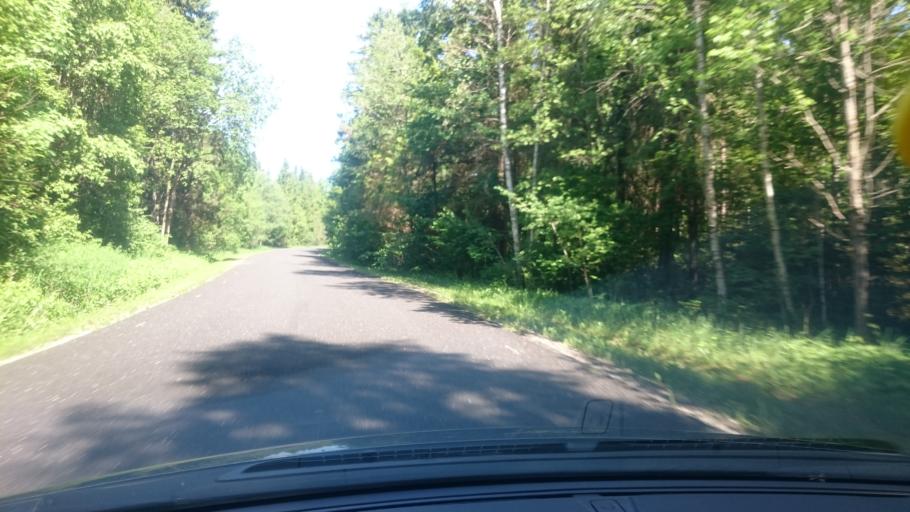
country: EE
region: Harju
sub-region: Rae vald
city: Vaida
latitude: 59.2102
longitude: 24.9504
